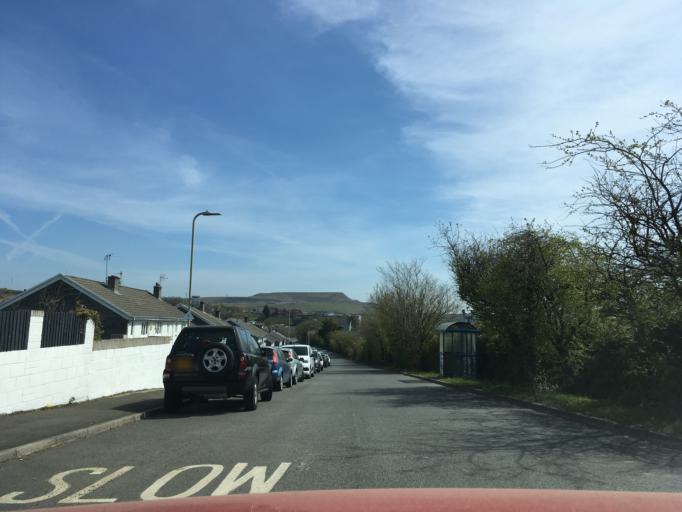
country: GB
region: Wales
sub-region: Merthyr Tydfil County Borough
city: Merthyr Tydfil
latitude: 51.7712
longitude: -3.3634
